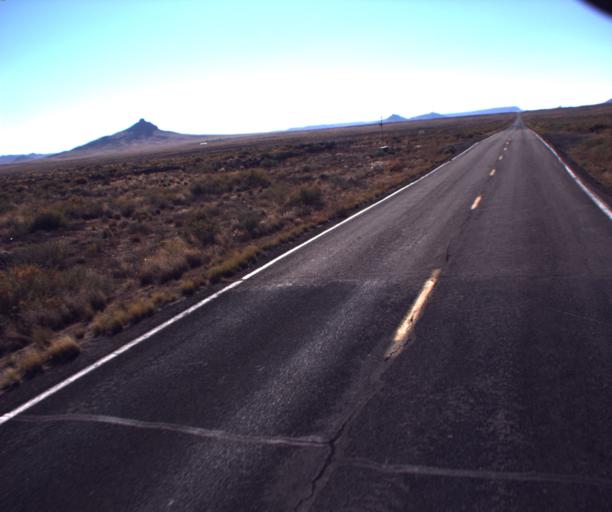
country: US
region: Arizona
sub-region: Navajo County
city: Dilkon
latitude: 35.5771
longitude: -110.4625
